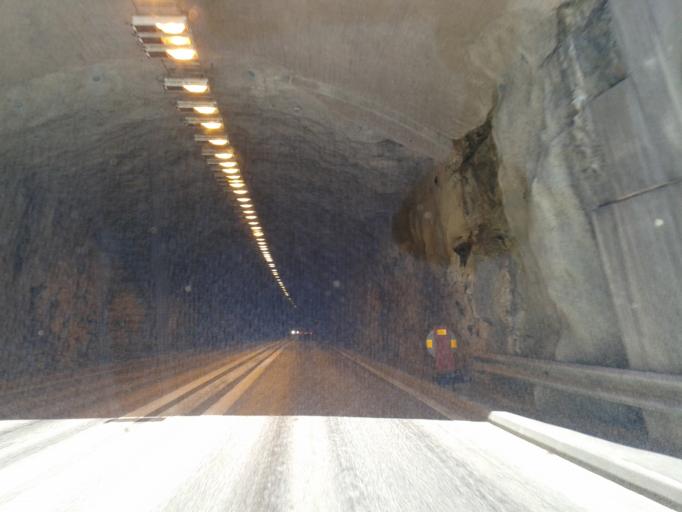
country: SE
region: Vaestra Goetaland
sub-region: Orust
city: Henan
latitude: 58.2975
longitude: 11.7011
